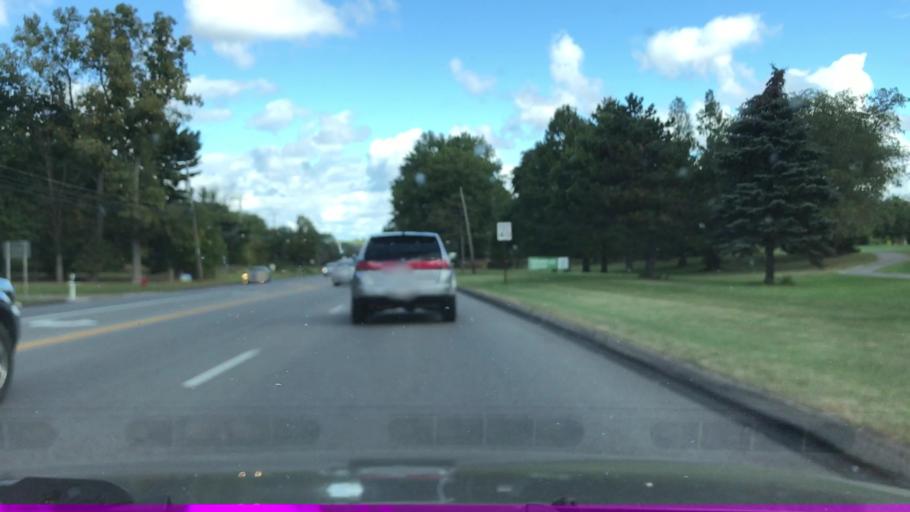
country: US
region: Ohio
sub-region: Lake County
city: Wickliffe
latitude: 41.5901
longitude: -81.4395
